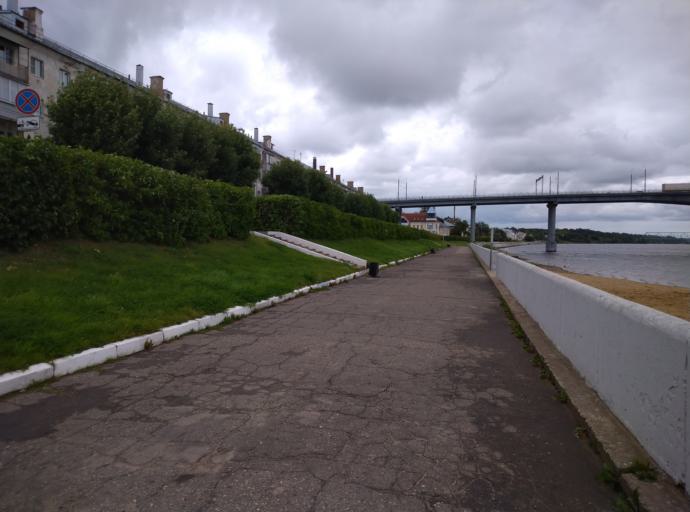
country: RU
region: Kostroma
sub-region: Kostromskoy Rayon
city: Kostroma
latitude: 57.7570
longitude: 40.9402
